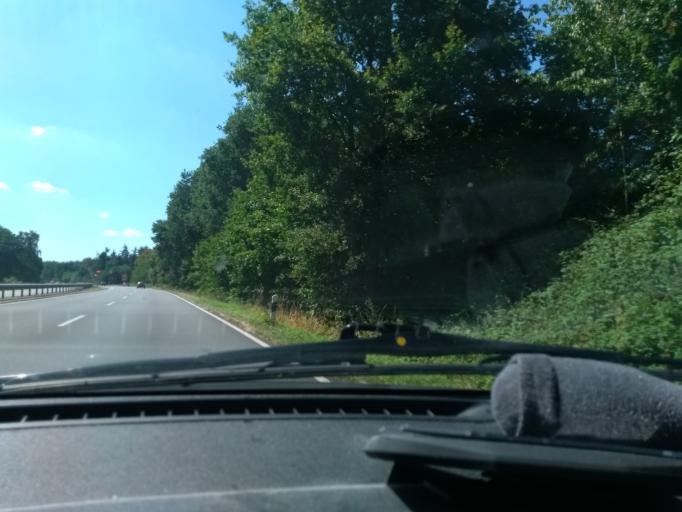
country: DE
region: Lower Saxony
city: Meppen
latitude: 52.6770
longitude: 7.3031
